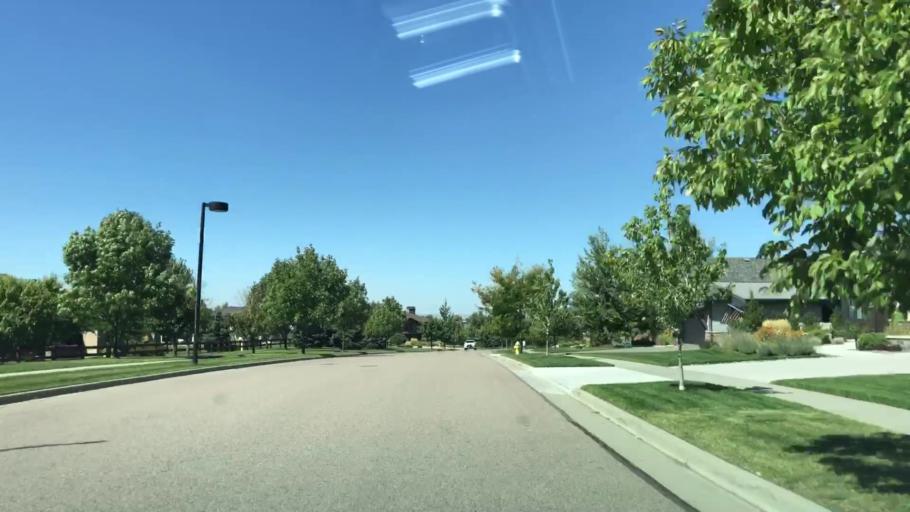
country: US
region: Colorado
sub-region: Weld County
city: Windsor
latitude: 40.5313
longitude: -104.9568
